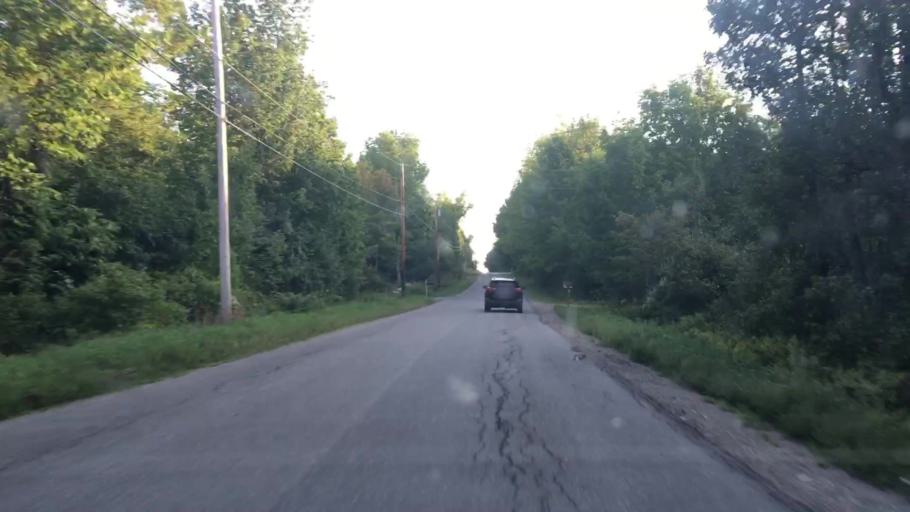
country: US
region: Maine
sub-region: Waldo County
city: Frankfort
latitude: 44.6818
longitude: -68.9122
